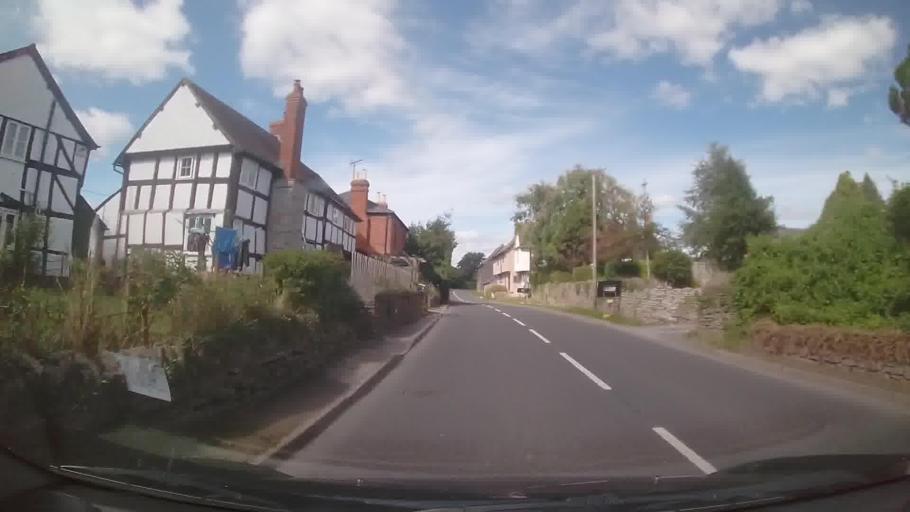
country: GB
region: England
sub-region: Herefordshire
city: Kinnersley
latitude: 52.1408
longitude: -3.0088
